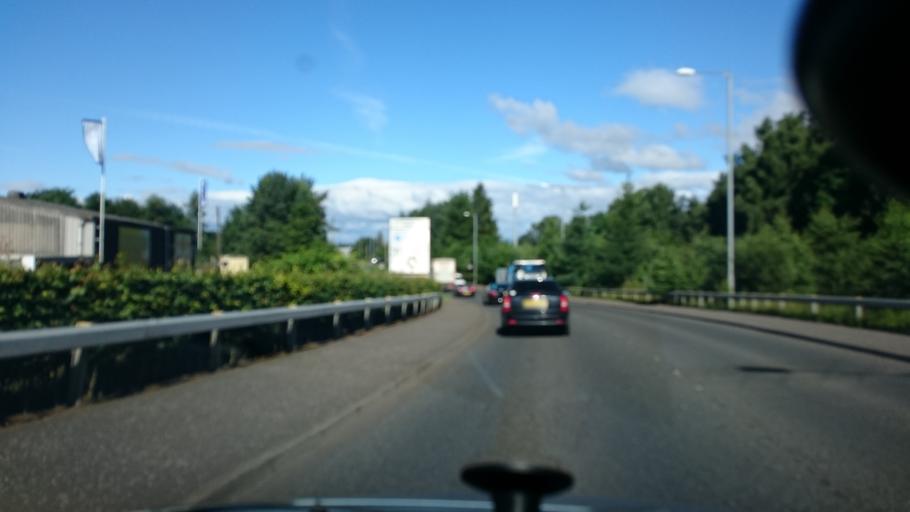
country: GB
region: Scotland
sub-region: Clackmannanshire
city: Alloa
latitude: 56.1151
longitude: -3.7699
